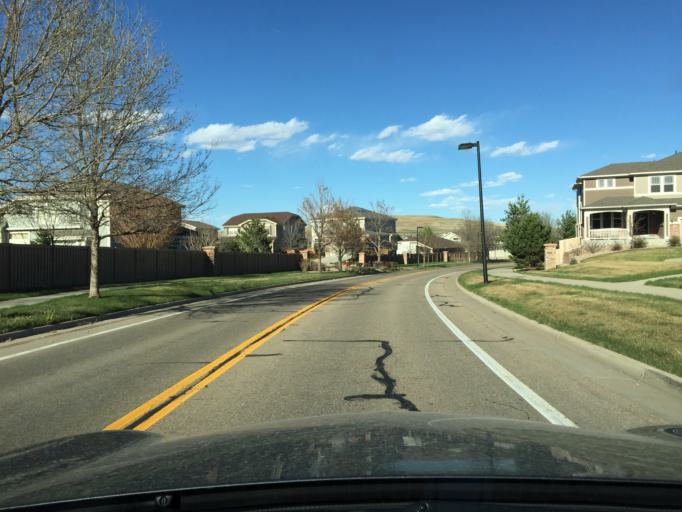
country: US
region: Colorado
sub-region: Boulder County
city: Erie
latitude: 40.0096
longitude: -105.0281
